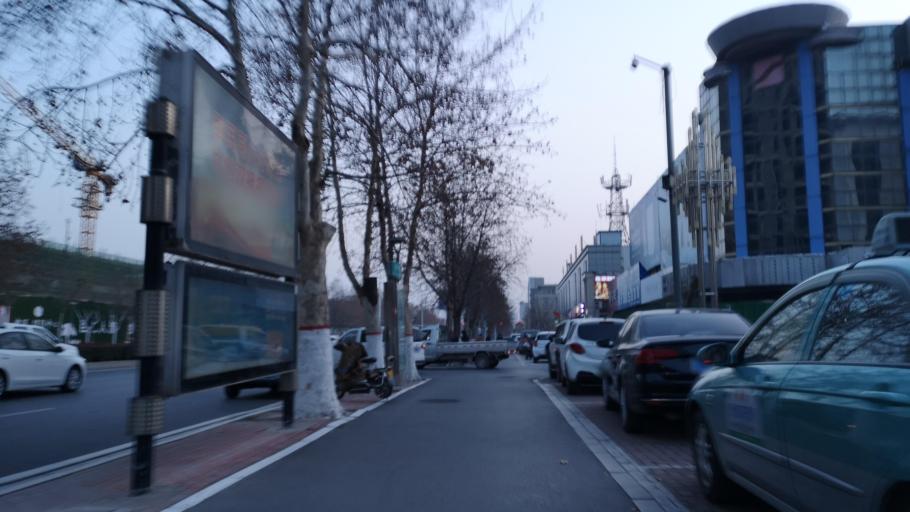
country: CN
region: Henan Sheng
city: Zhongyuanlu
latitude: 35.7747
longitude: 115.0701
